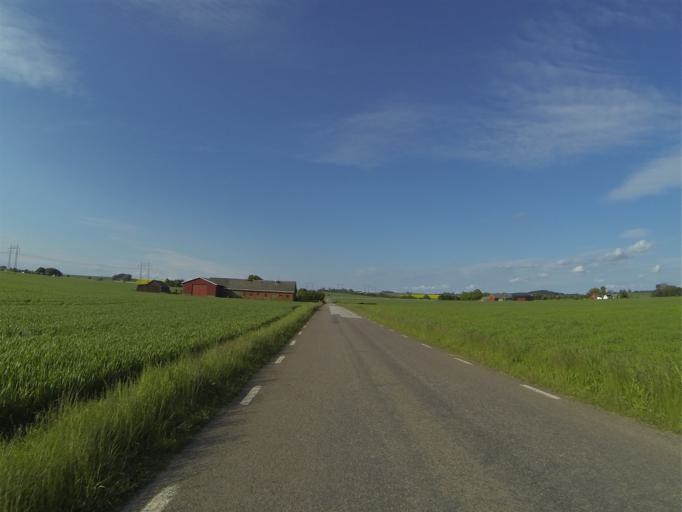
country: SE
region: Skane
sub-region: Staffanstorps Kommun
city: Staffanstorp
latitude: 55.6752
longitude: 13.2805
